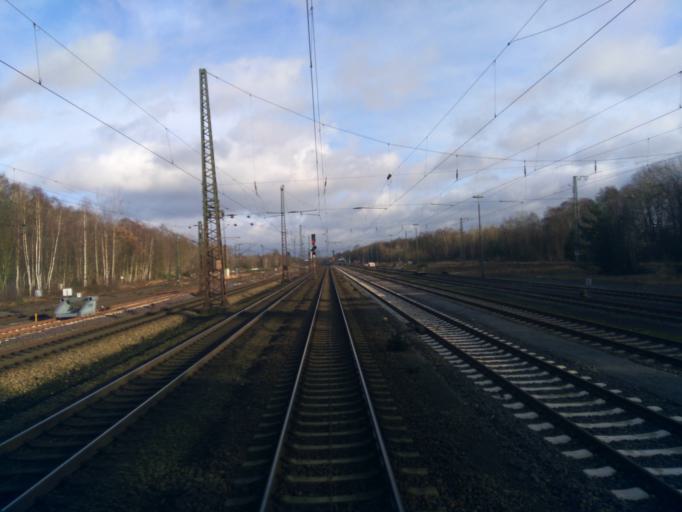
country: DE
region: Lower Saxony
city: Rotenburg
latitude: 53.1106
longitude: 9.3766
